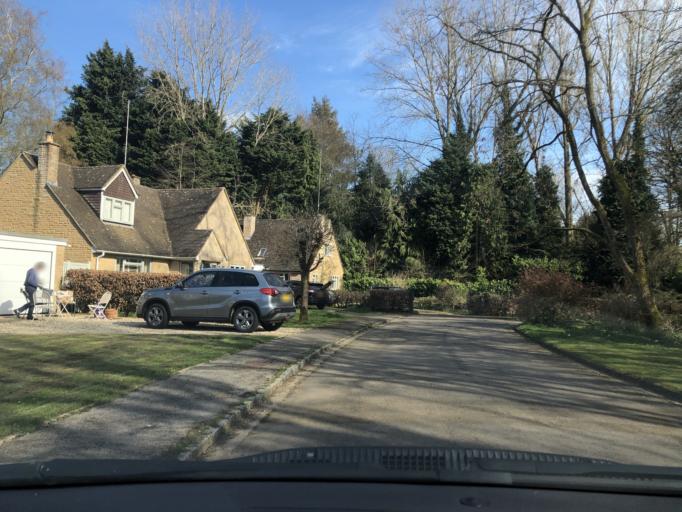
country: GB
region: England
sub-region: Oxfordshire
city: Hook Norton
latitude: 51.9958
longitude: -1.4902
